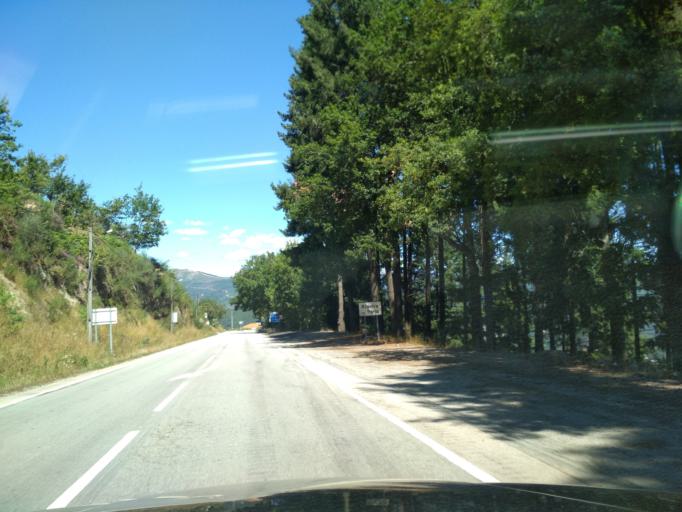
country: PT
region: Vila Real
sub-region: Ribeira de Pena
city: Ribeira de Pena
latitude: 41.5182
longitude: -7.8061
